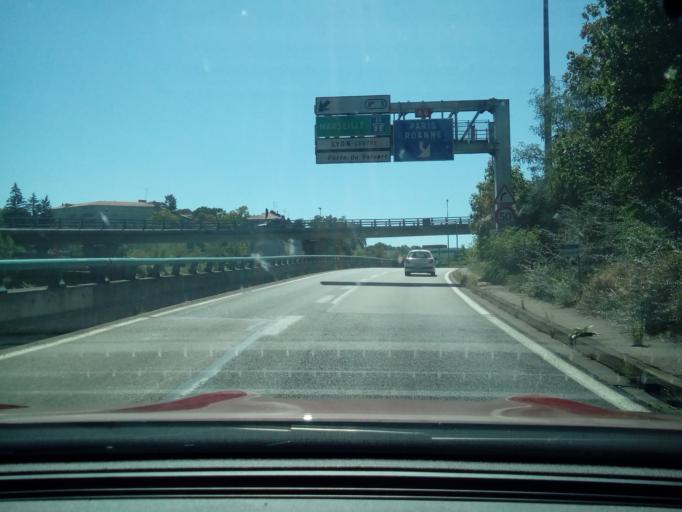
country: FR
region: Rhone-Alpes
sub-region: Departement du Rhone
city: Ecully
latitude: 45.7751
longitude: 4.7828
